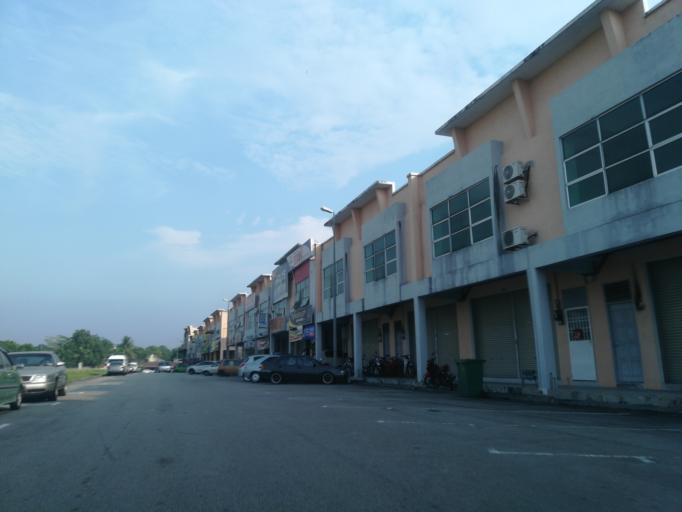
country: MY
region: Kedah
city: Kulim
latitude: 5.3889
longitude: 100.5727
